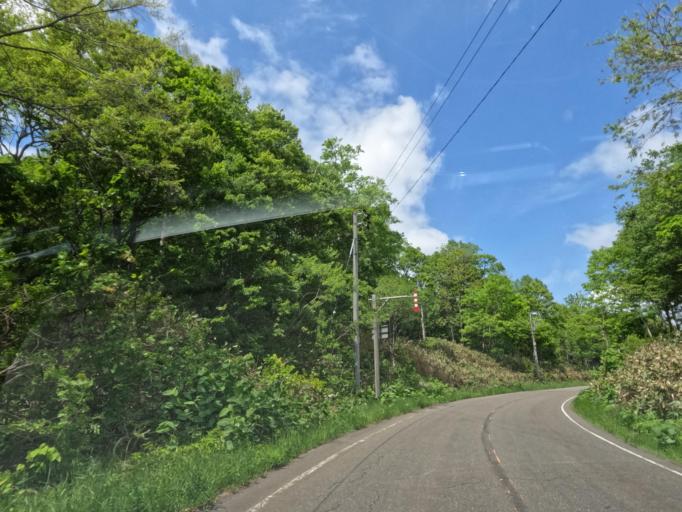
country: JP
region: Hokkaido
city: Tobetsu
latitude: 43.5039
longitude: 141.6057
